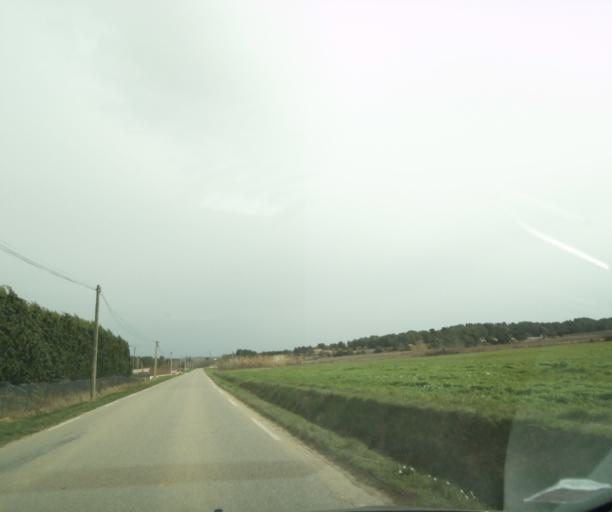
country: FR
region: Provence-Alpes-Cote d'Azur
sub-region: Departement des Bouches-du-Rhone
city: Trets
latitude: 43.4685
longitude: 5.7077
